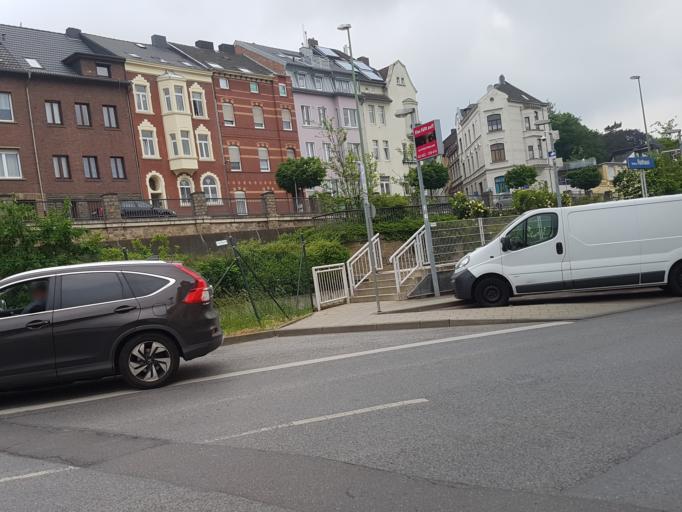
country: DE
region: North Rhine-Westphalia
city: Stolberg
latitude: 50.7683
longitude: 6.2304
